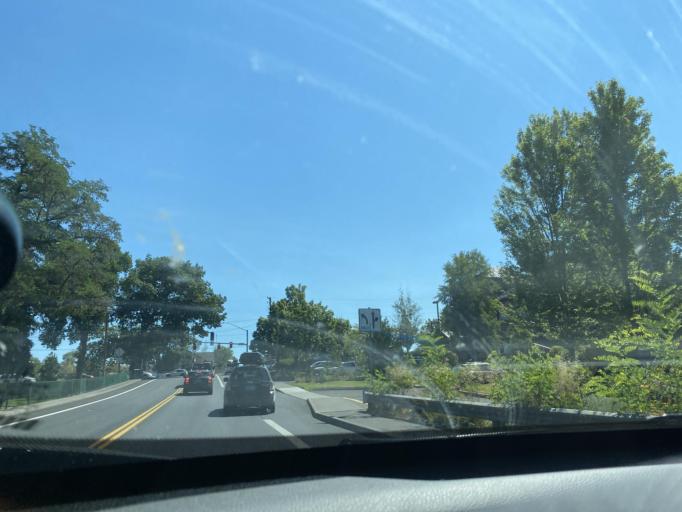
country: US
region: Oregon
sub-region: Deschutes County
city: Bend
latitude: 44.0642
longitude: -121.3102
